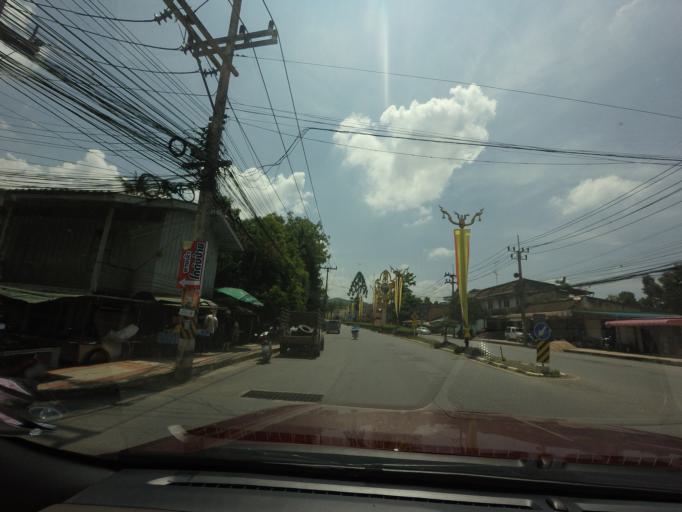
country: TH
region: Yala
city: Betong
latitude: 5.7784
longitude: 101.0739
